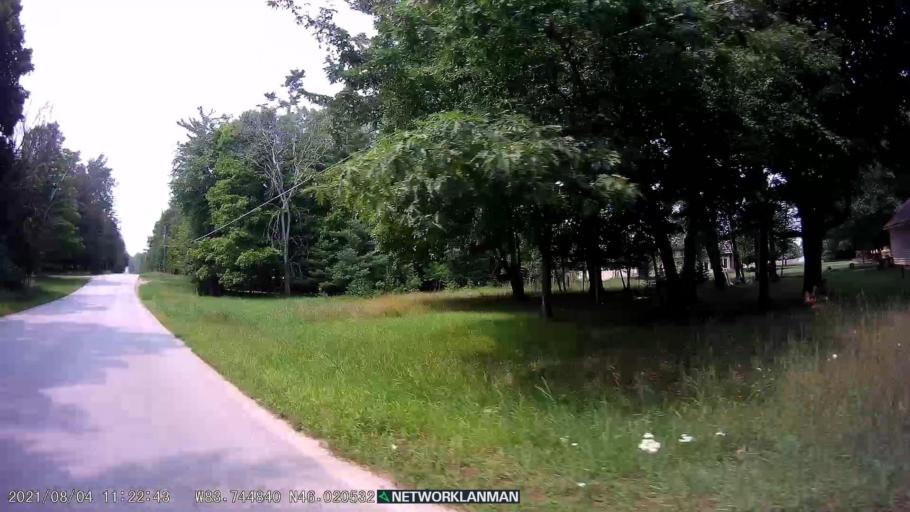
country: CA
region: Ontario
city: Thessalon
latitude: 46.0207
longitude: -83.7452
